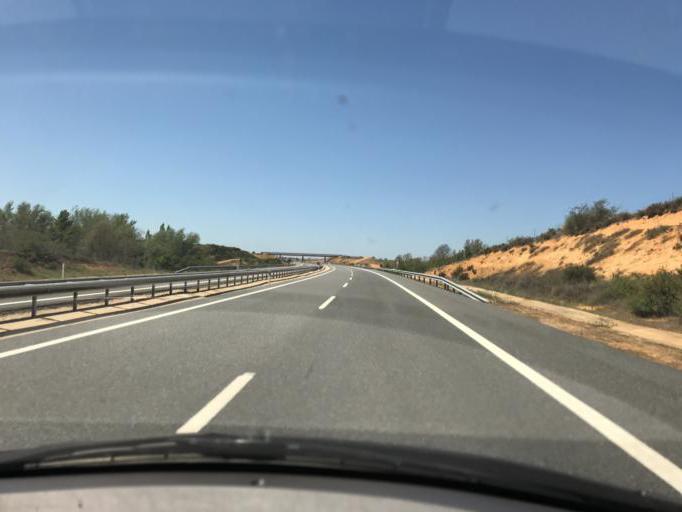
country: ES
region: Castille and Leon
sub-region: Provincia de Leon
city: Valverde de la Virgen
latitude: 42.5583
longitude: -5.6856
